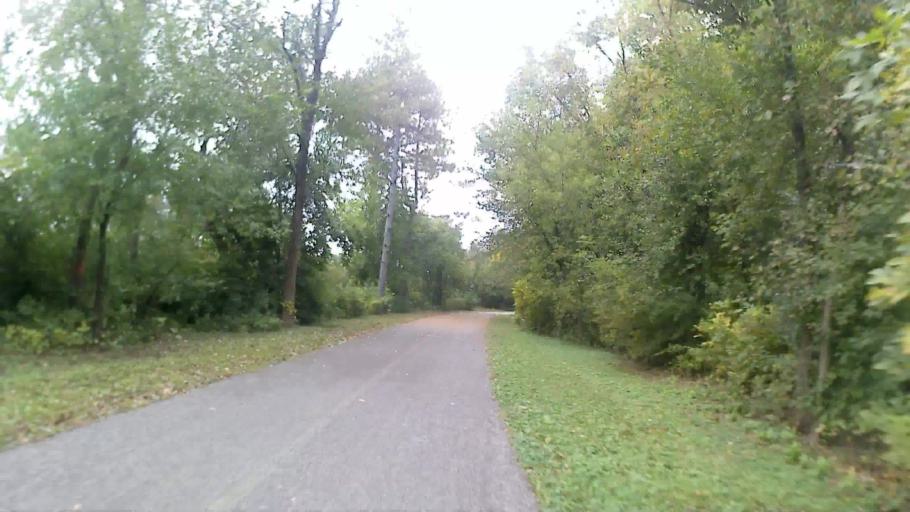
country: US
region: Illinois
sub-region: Kane County
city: Montgomery
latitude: 41.7456
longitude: -88.3562
